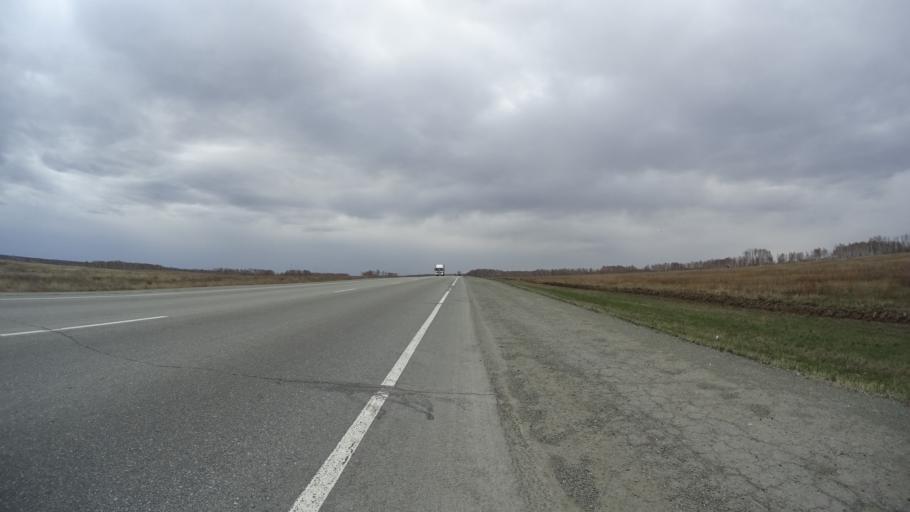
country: RU
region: Chelyabinsk
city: Yemanzhelinsk
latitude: 54.7062
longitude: 61.2568
